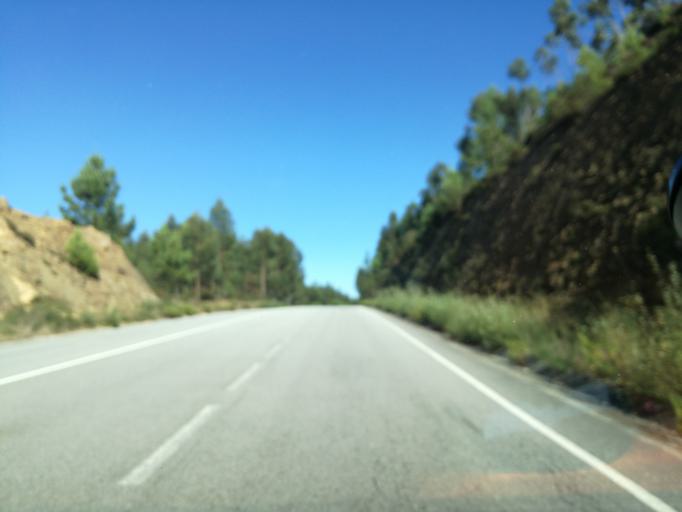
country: PT
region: Porto
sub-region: Pacos de Ferreira
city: Seroa
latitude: 41.2705
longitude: -8.4379
